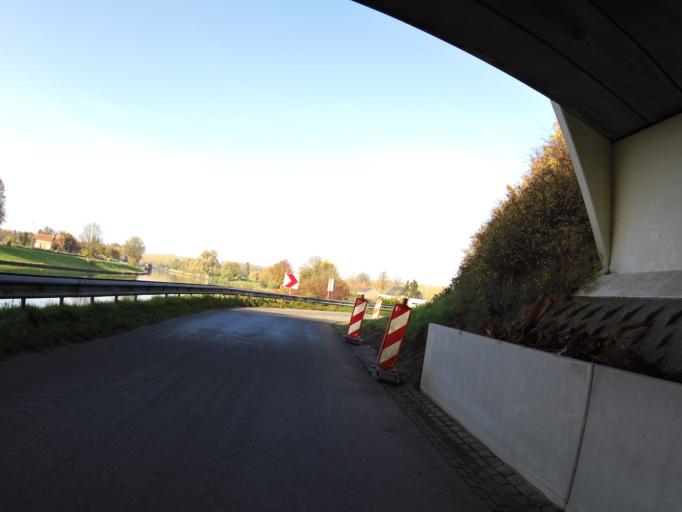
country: NL
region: North Brabant
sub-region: Gemeente 's-Hertogenbosch
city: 's-Hertogenbosch
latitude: 51.7149
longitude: 5.2766
